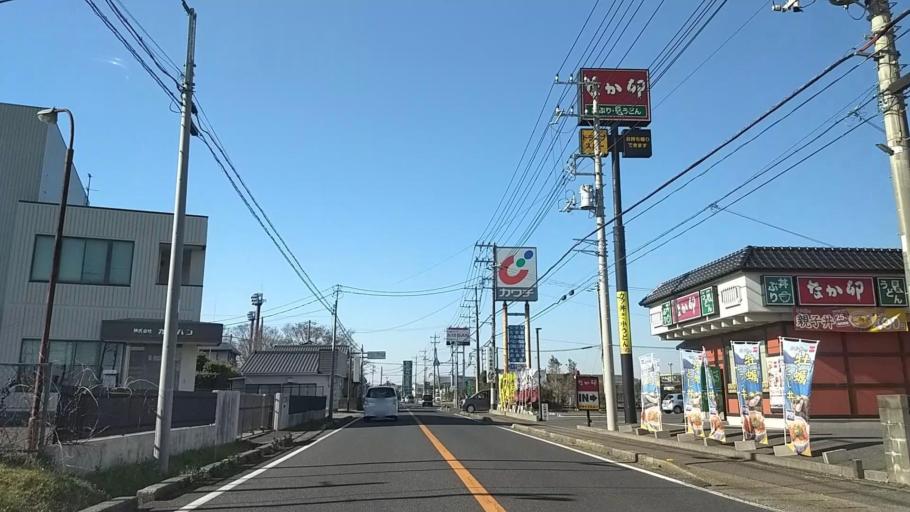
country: JP
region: Chiba
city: Asahi
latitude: 35.7236
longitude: 140.6313
